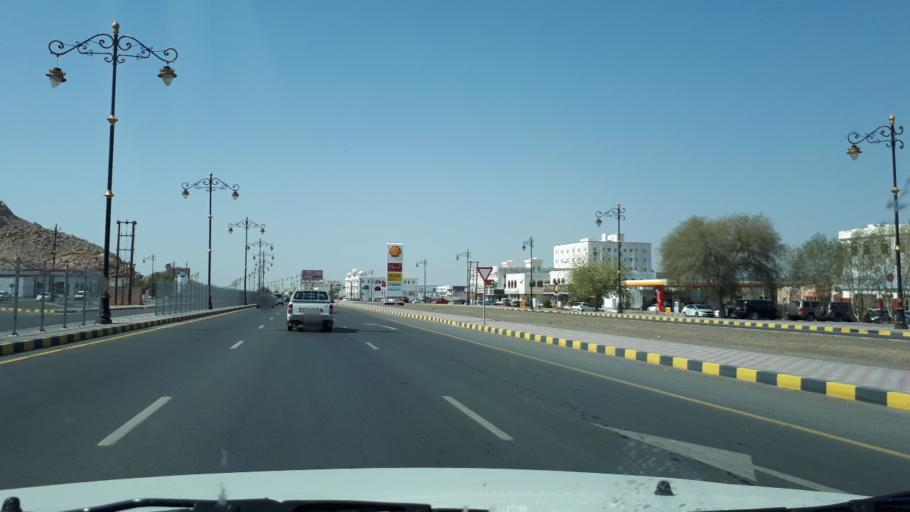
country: OM
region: Muhafazat ad Dakhiliyah
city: Nizwa
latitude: 22.9054
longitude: 57.5336
